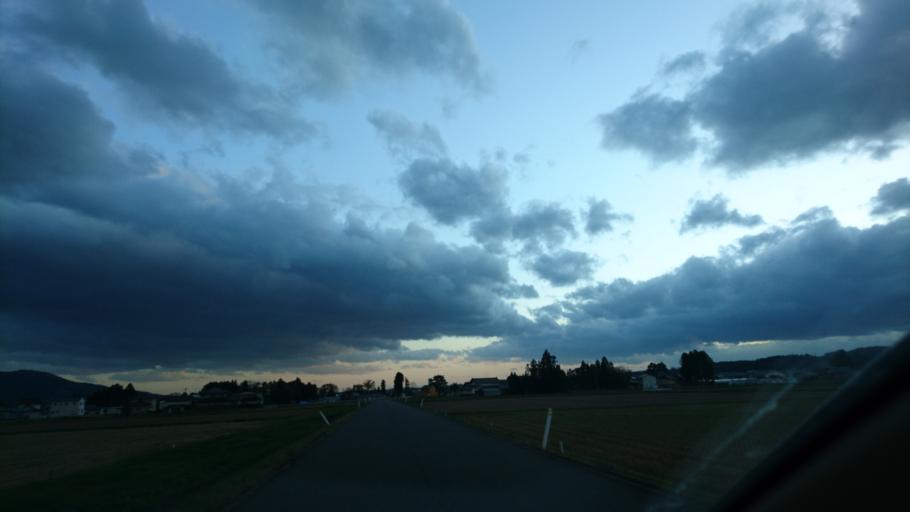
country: JP
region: Iwate
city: Mizusawa
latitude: 39.0676
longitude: 141.1414
